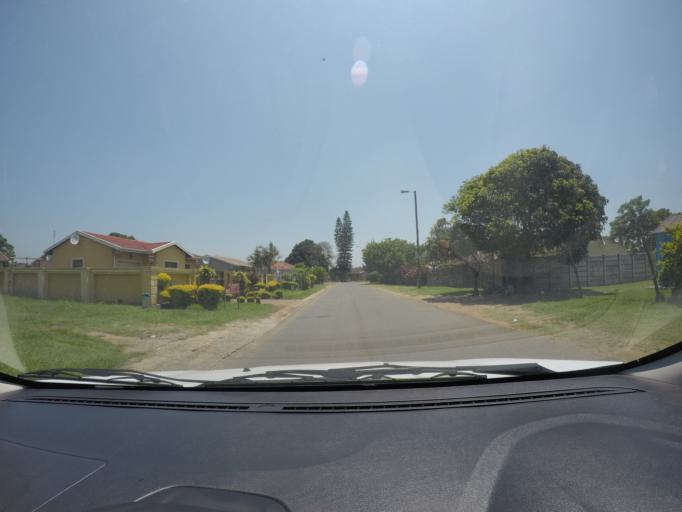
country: ZA
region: KwaZulu-Natal
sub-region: uThungulu District Municipality
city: eSikhawini
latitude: -28.8878
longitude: 31.8884
